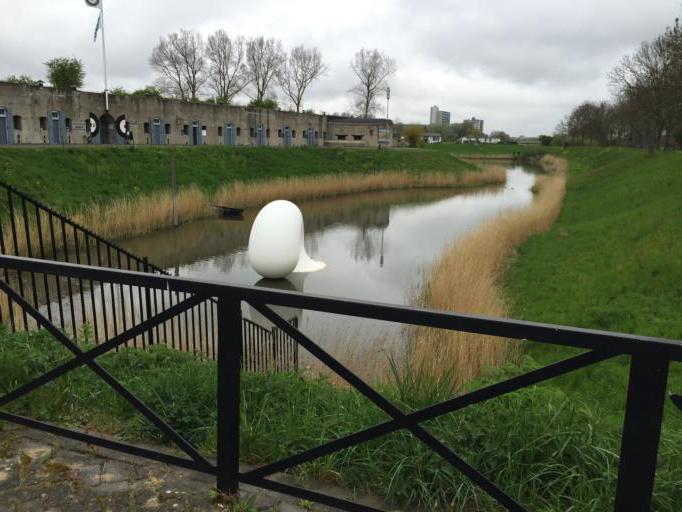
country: NL
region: North Holland
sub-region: Gemeente Haarlemmermeer
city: Hoofddorp
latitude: 52.3470
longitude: 4.6715
